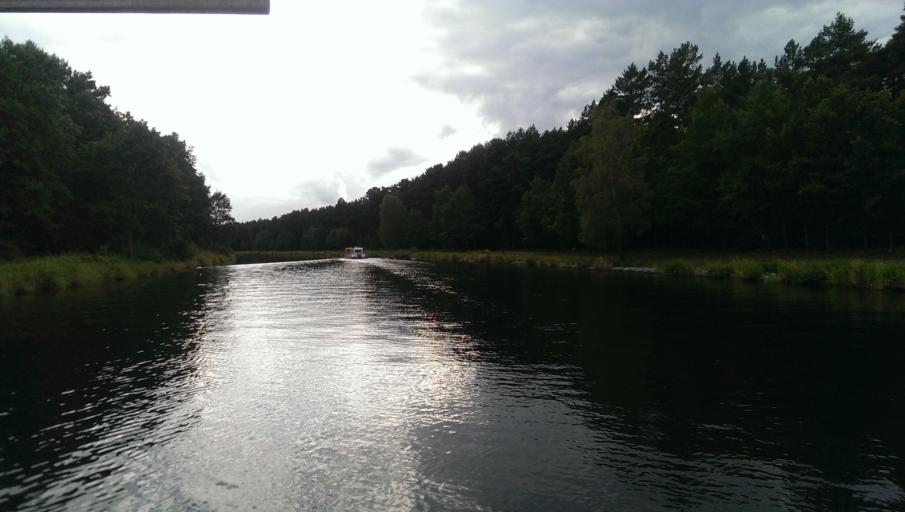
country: DE
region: Brandenburg
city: Oranienburg
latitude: 52.7886
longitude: 13.2828
